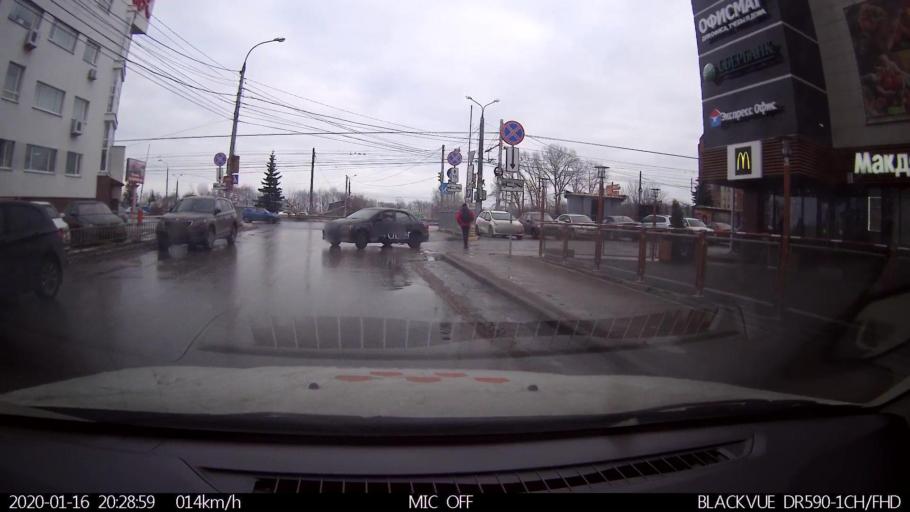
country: RU
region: Nizjnij Novgorod
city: Bor
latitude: 56.3155
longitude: 44.0668
